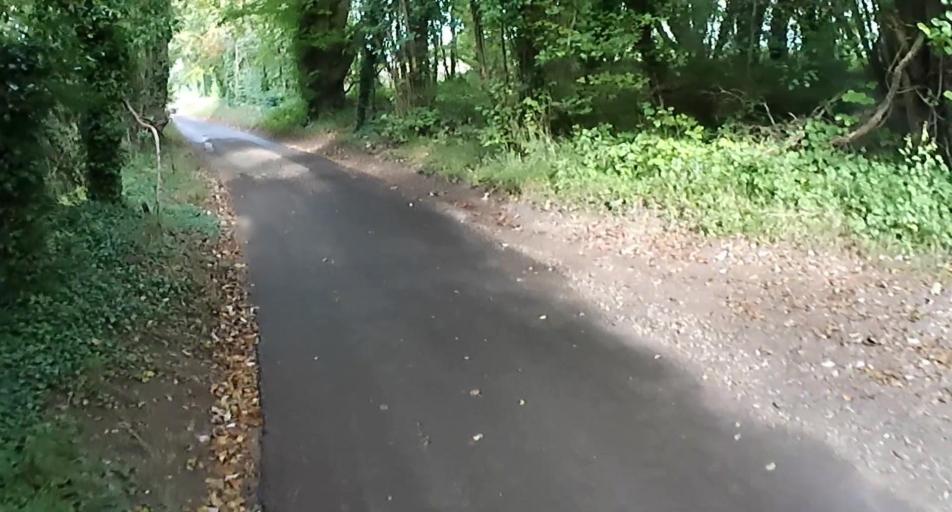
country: GB
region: England
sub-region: Hampshire
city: Kingsclere
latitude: 51.2772
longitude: -1.1982
